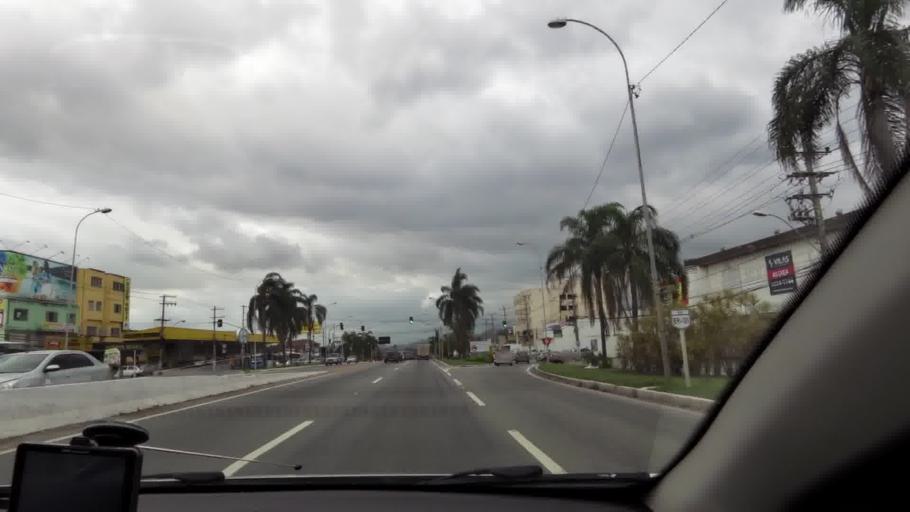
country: BR
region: Espirito Santo
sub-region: Vila Velha
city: Vila Velha
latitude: -20.2351
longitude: -40.2763
